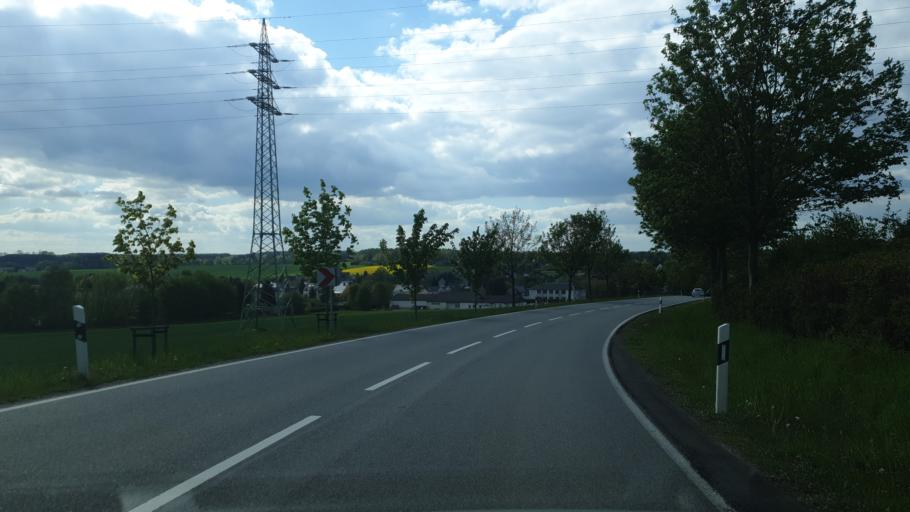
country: DE
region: Saxony
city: Lugau
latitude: 50.7051
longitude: 12.7422
